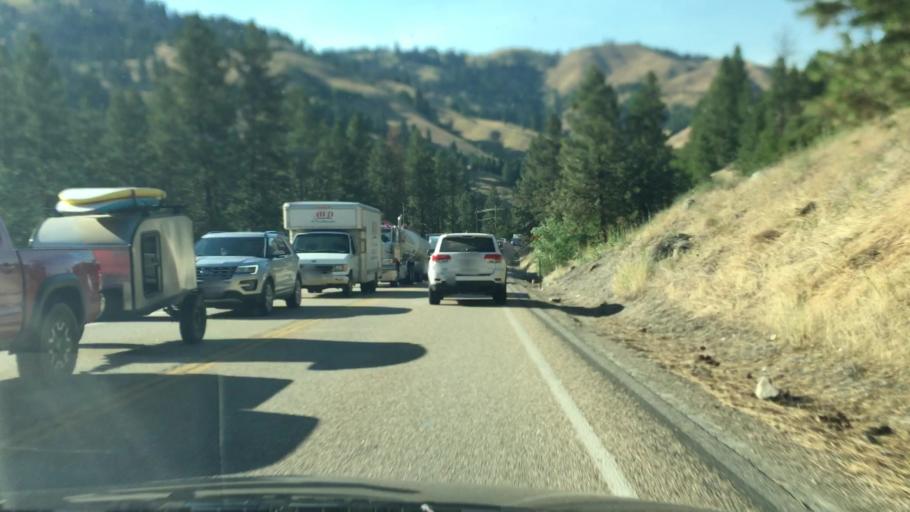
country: US
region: Idaho
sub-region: Boise County
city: Idaho City
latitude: 44.0479
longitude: -116.1317
